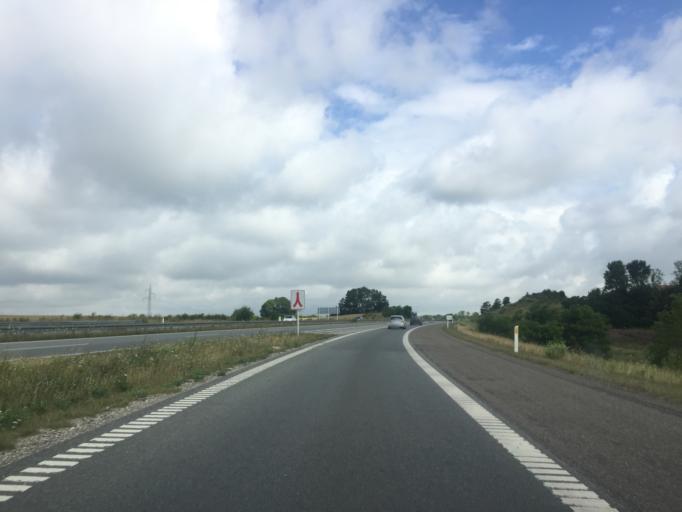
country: DK
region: South Denmark
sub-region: Svendborg Kommune
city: Svendborg
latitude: 55.0749
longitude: 10.5760
